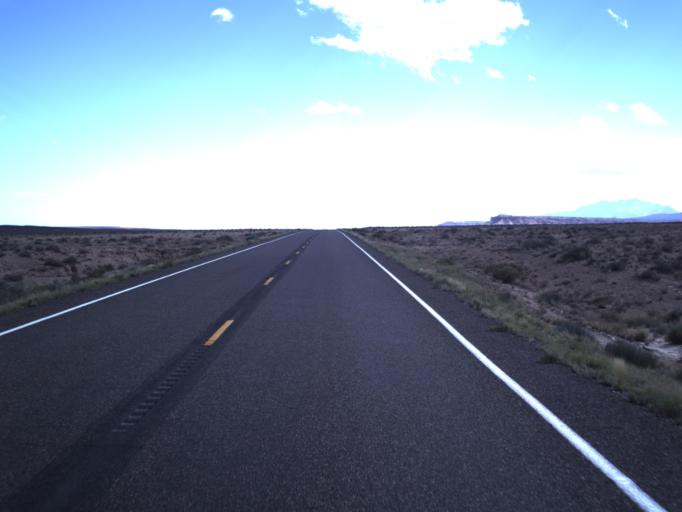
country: US
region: Utah
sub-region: Emery County
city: Ferron
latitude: 38.2768
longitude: -110.6612
